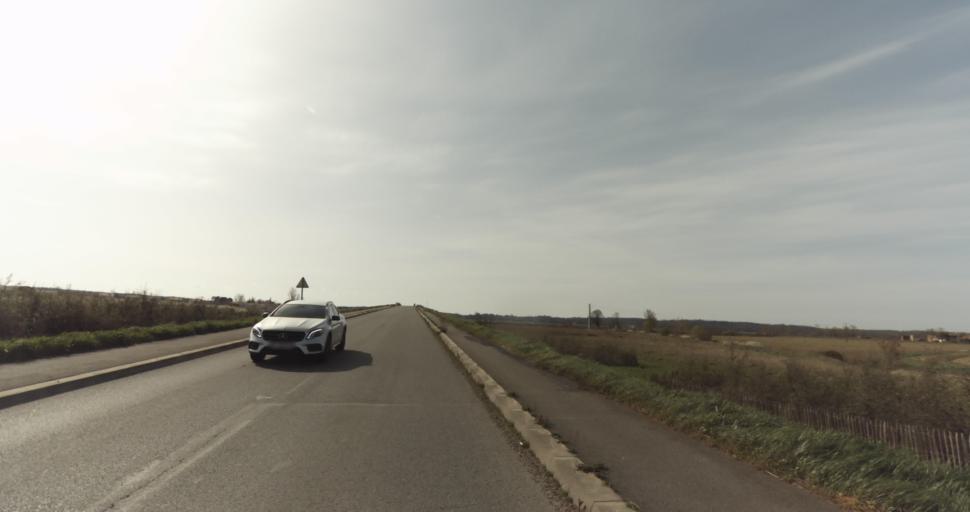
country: FR
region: Midi-Pyrenees
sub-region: Departement de la Haute-Garonne
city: Buzet-sur-Tarn
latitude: 43.7679
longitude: 1.6563
